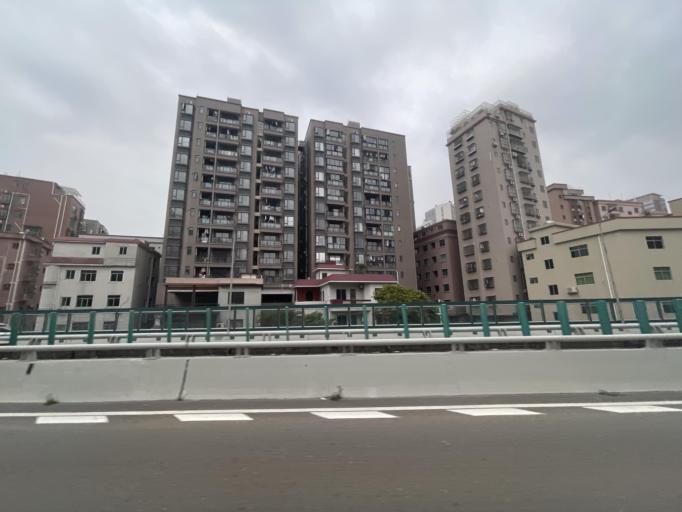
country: CN
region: Guangdong
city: Humen
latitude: 22.8060
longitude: 113.6810
